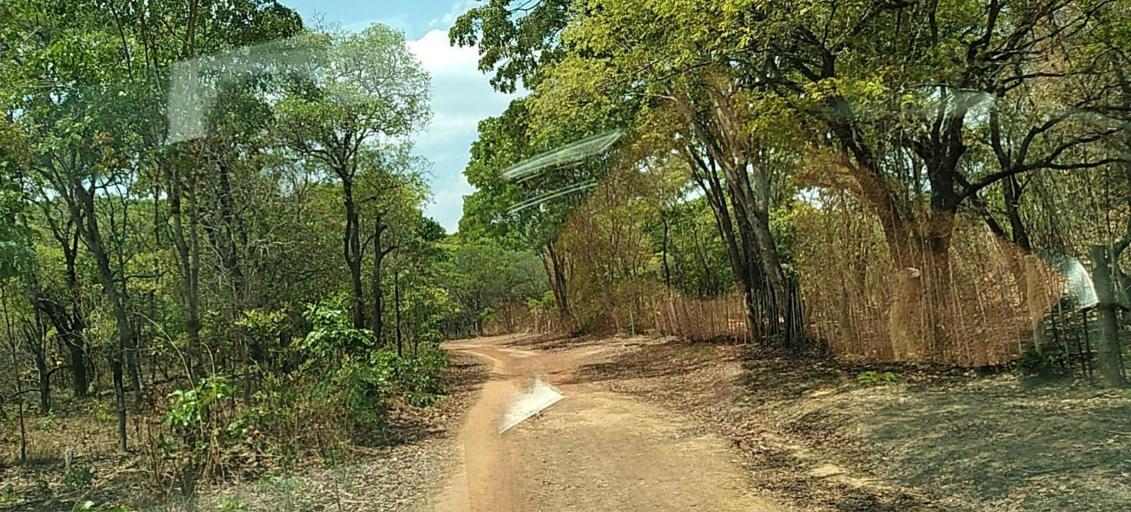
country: ZM
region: Copperbelt
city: Chililabombwe
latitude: -12.4827
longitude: 27.6429
